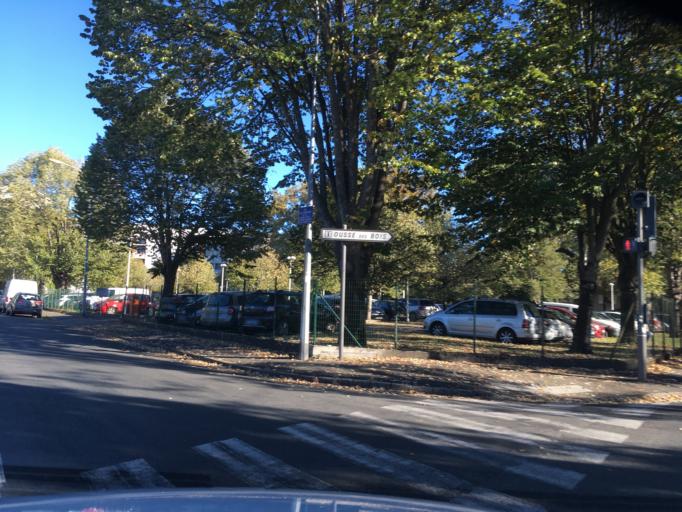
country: FR
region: Aquitaine
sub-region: Departement des Pyrenees-Atlantiques
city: Pau
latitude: 43.3049
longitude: -0.3523
